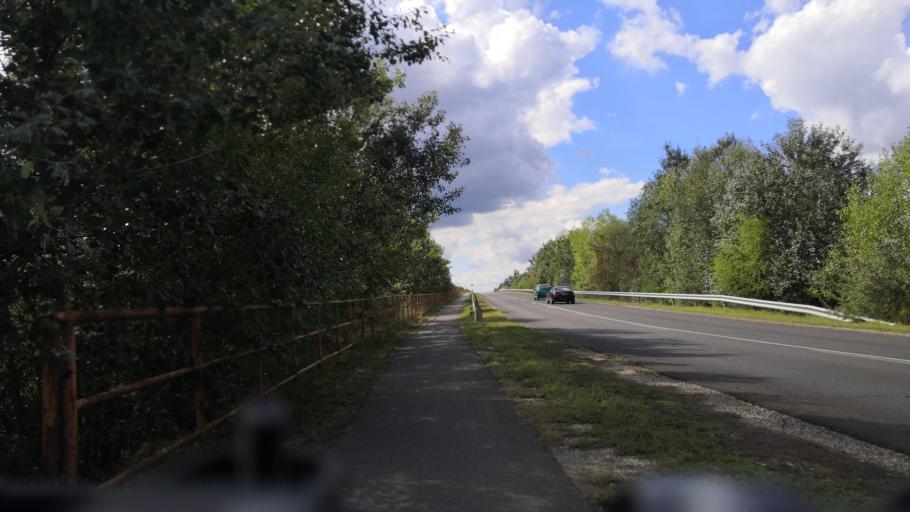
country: HU
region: Csongrad
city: Domaszek
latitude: 46.2765
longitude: 20.0441
